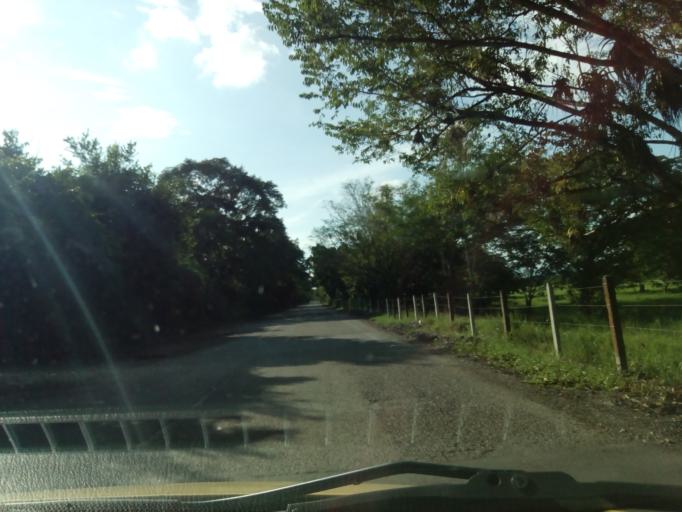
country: CO
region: Boyaca
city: Puerto Boyaca
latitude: 5.9386
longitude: -74.5552
